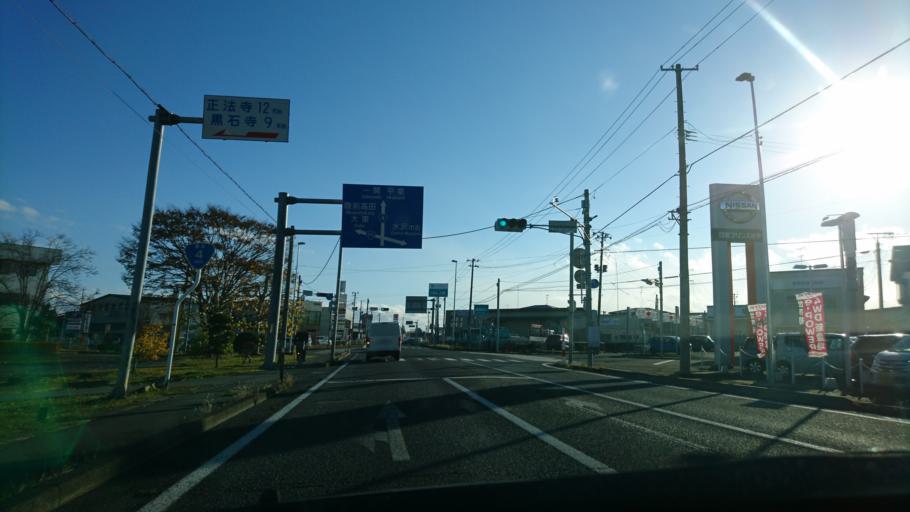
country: JP
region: Iwate
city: Mizusawa
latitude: 39.1337
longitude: 141.1501
